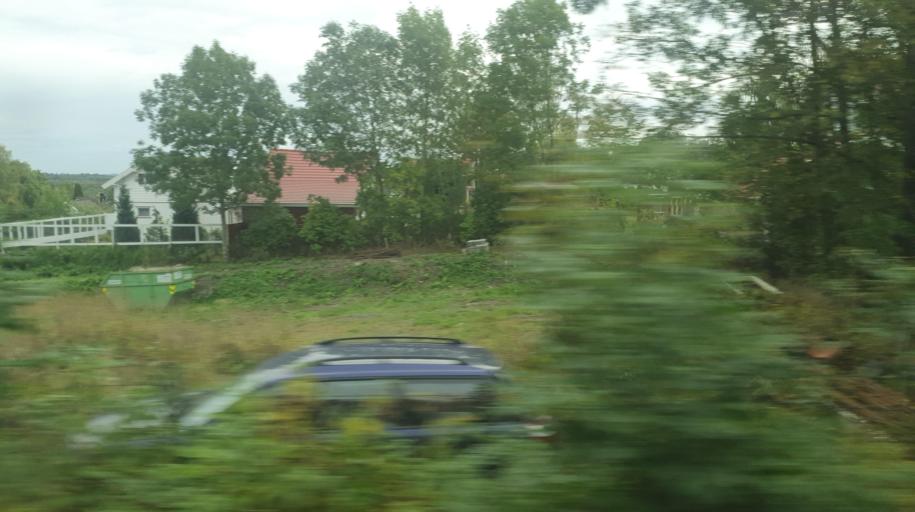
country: NO
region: Vestfold
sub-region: Horten
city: Skoppum
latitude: 59.3858
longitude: 10.4094
